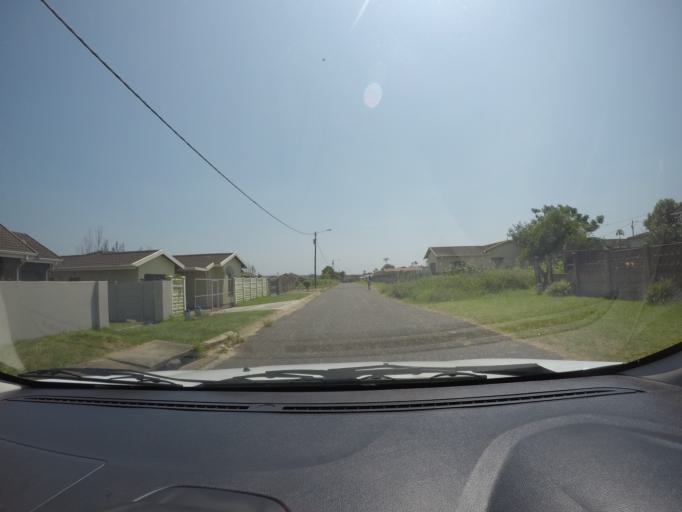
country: ZA
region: KwaZulu-Natal
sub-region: uThungulu District Municipality
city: eSikhawini
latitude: -28.8658
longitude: 31.9182
